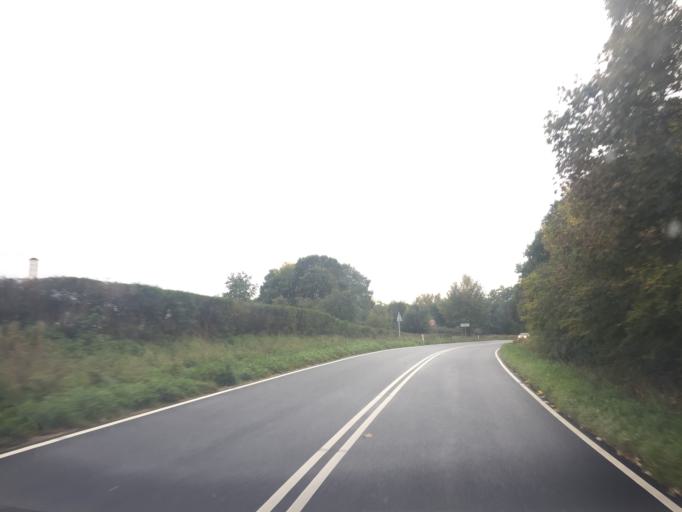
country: DK
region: Capital Region
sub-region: Allerod Kommune
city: Lynge
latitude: 55.8215
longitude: 12.2708
